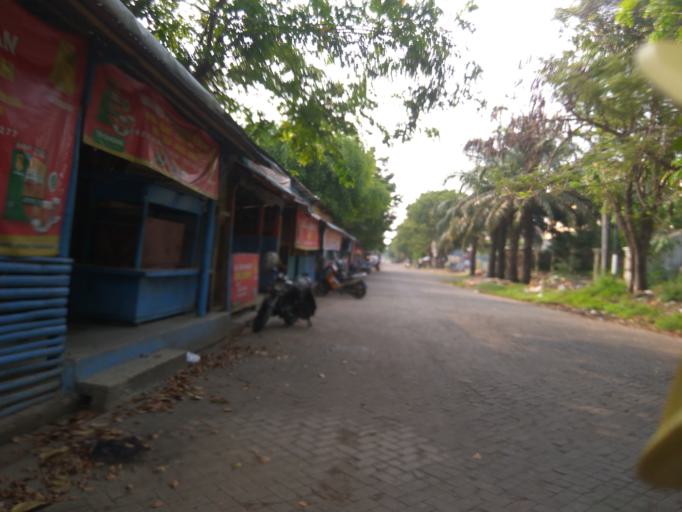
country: ID
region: Central Java
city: Semarang
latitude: -6.9702
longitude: 110.3966
